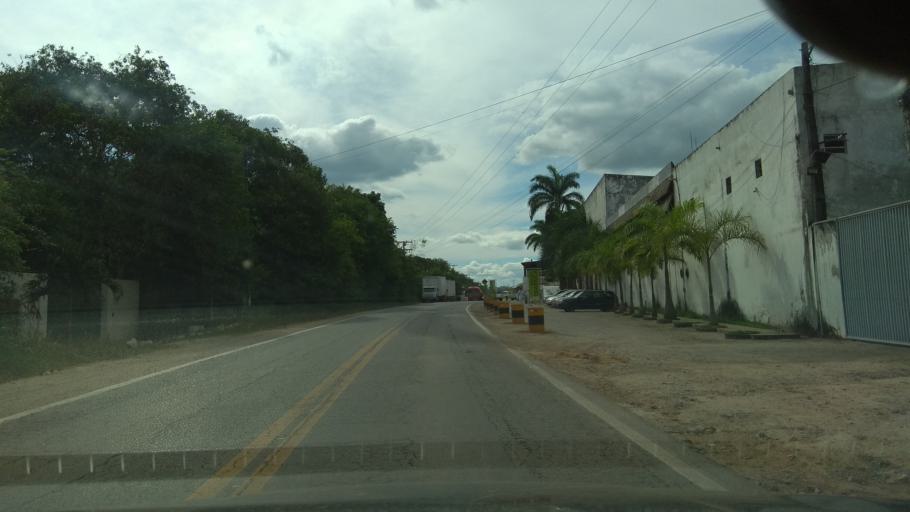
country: BR
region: Bahia
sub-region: Ipiau
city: Ipiau
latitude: -14.1184
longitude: -39.7713
